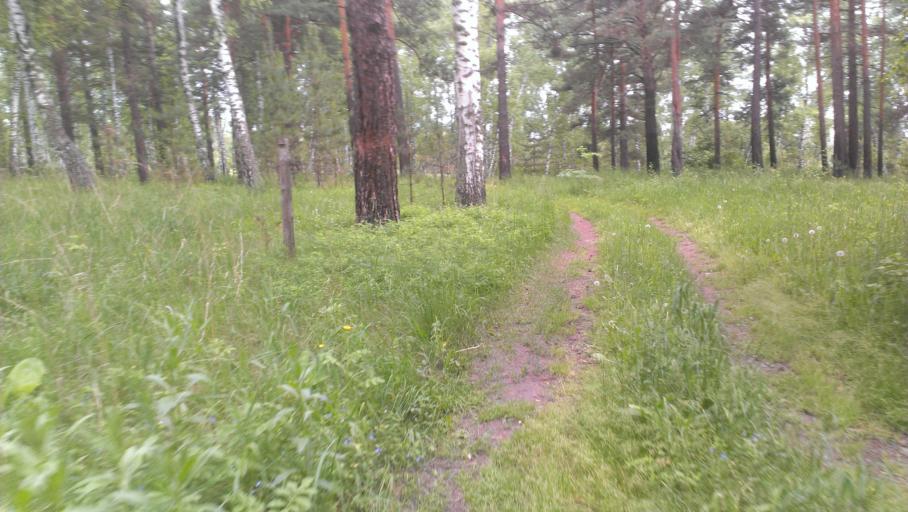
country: RU
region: Altai Krai
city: Sannikovo
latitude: 53.3384
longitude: 84.0504
